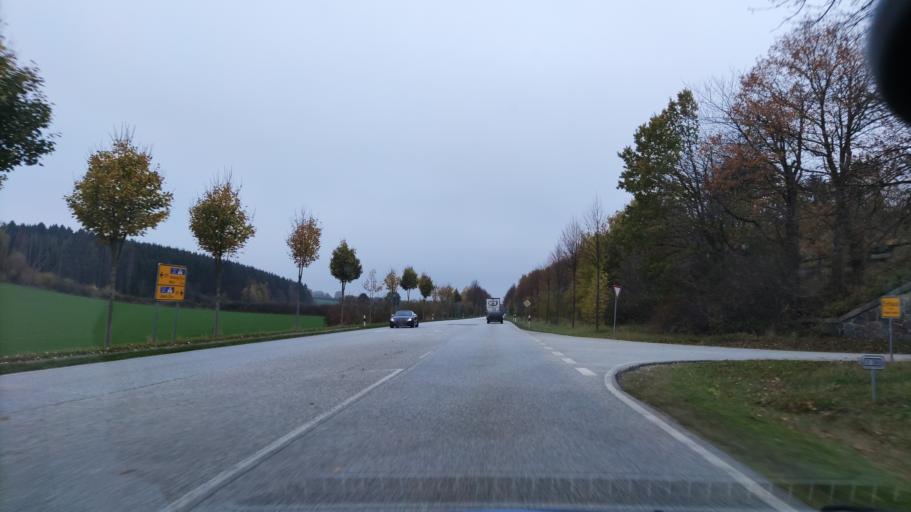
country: DE
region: Schleswig-Holstein
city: Einhaus
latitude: 53.7129
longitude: 10.7342
